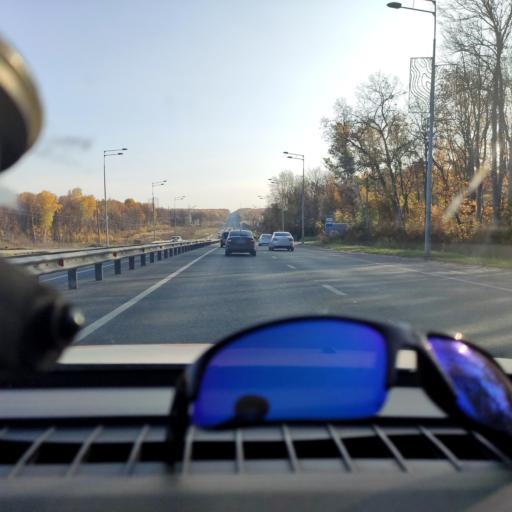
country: RU
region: Samara
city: Novosemeykino
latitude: 53.3412
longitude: 50.2327
